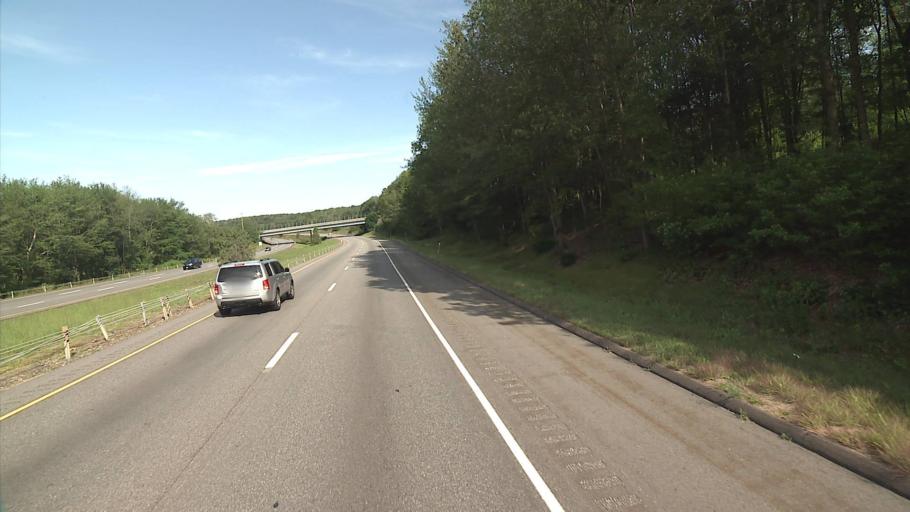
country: US
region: Connecticut
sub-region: New London County
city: Colchester
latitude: 41.5806
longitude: -72.3563
